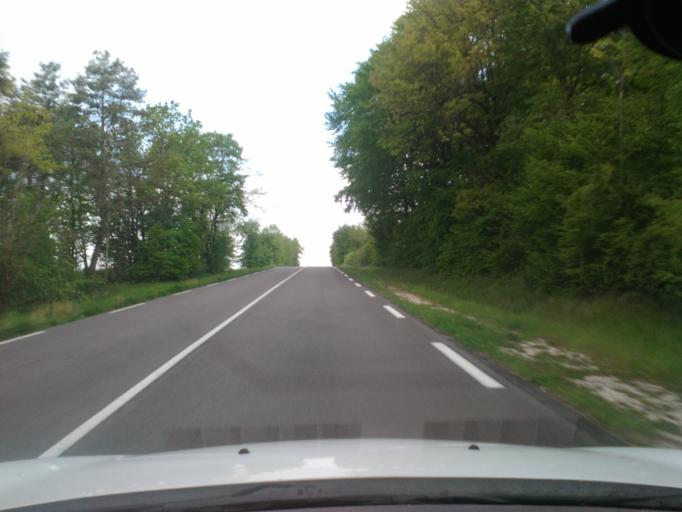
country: FR
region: Champagne-Ardenne
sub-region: Departement de la Haute-Marne
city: Lavilleneuve-au-Roi
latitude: 48.1947
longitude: 4.9511
